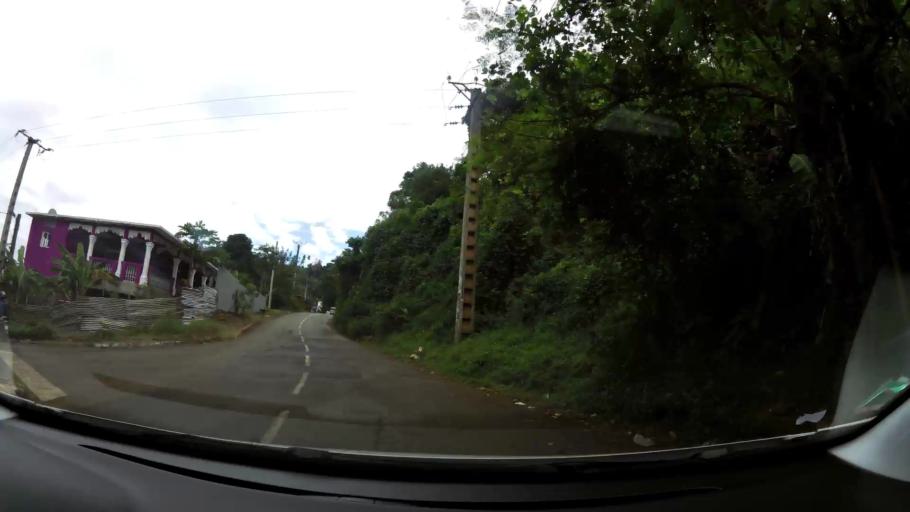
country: YT
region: Chiconi
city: Chiconi
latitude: -12.8393
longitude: 45.1213
